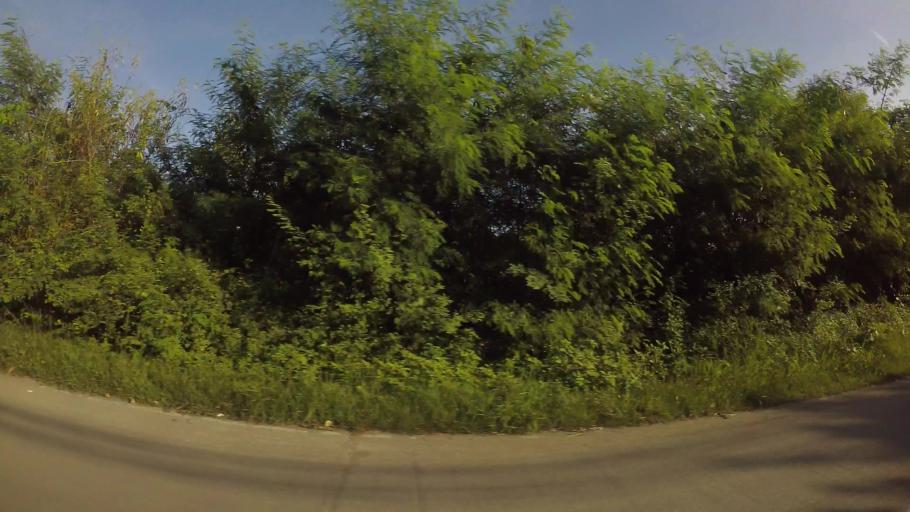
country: TH
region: Rayong
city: Rayong
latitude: 12.6839
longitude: 101.2910
